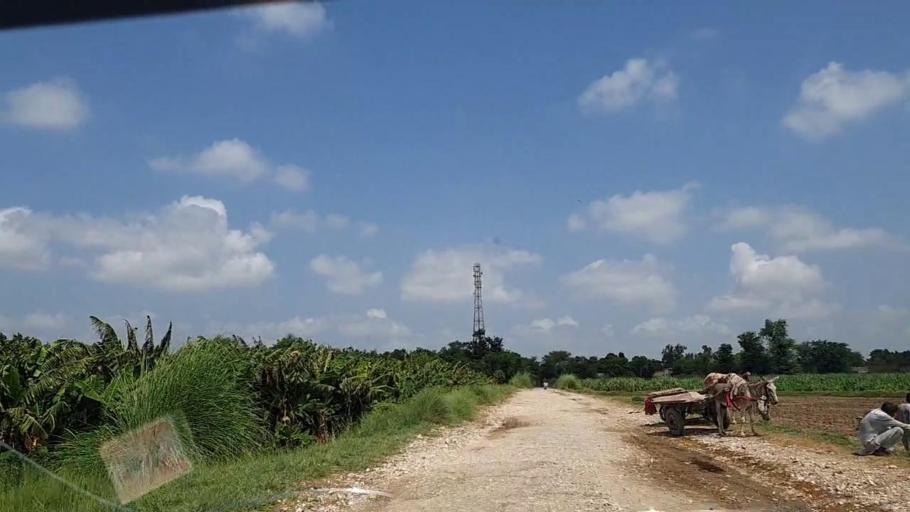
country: PK
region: Sindh
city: Tharu Shah
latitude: 26.9088
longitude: 68.0363
